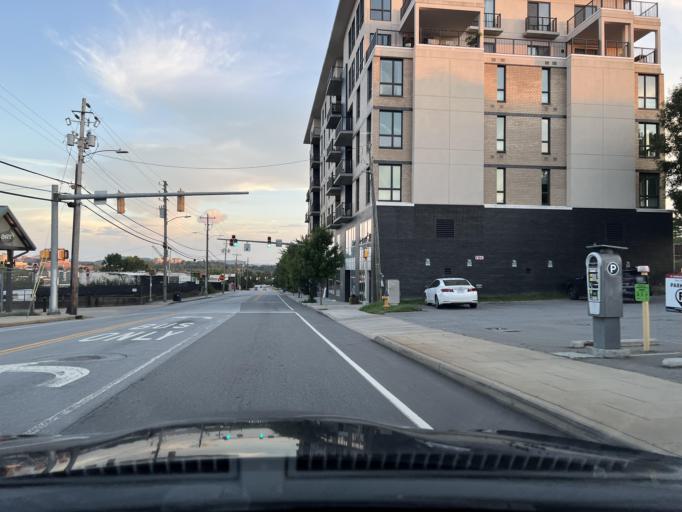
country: US
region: North Carolina
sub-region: Buncombe County
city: Asheville
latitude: 35.5932
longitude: -82.5564
